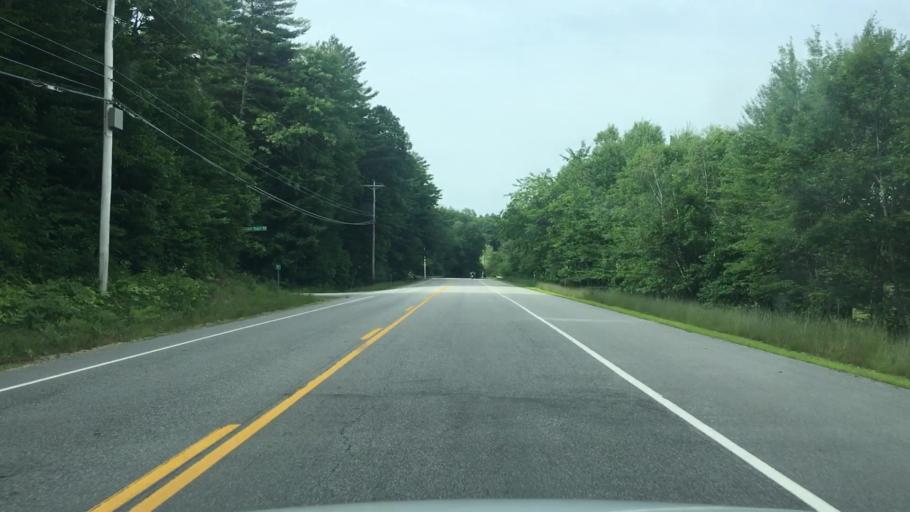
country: US
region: New Hampshire
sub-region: Carroll County
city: Sandwich
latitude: 43.8041
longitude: -71.3568
